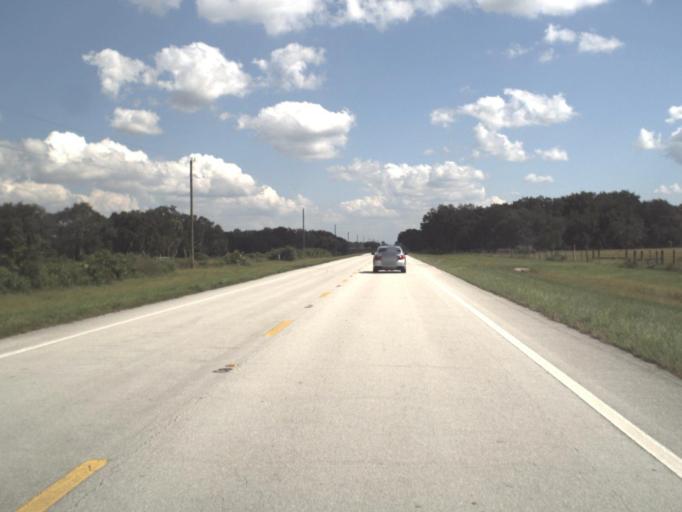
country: US
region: Florida
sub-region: Highlands County
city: Lake Placid
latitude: 27.3797
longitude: -81.1048
